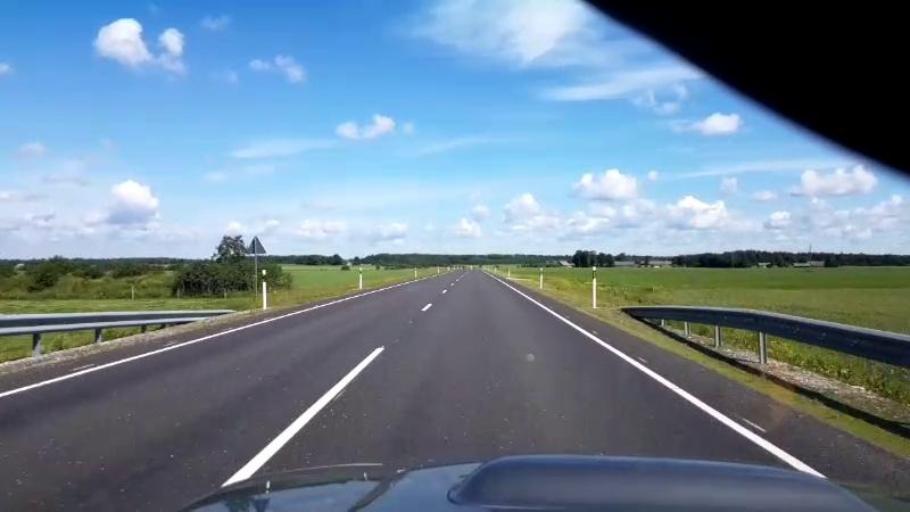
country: EE
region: Jaervamaa
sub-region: Jaerva-Jaani vald
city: Jarva-Jaani
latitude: 59.1435
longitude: 25.7712
